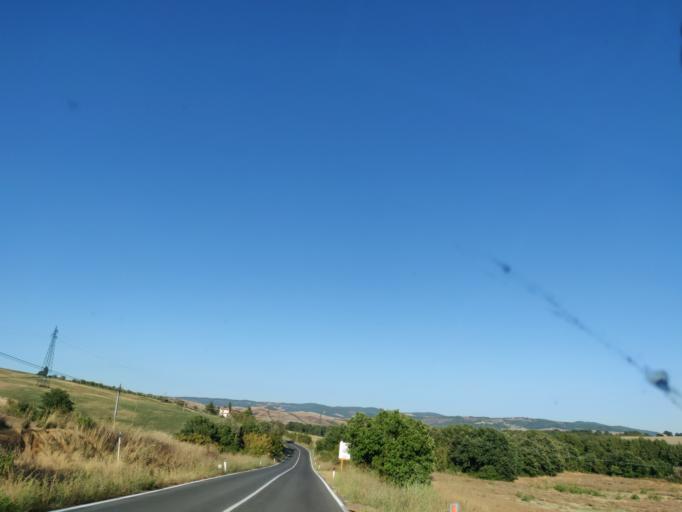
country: IT
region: Tuscany
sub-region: Provincia di Grosseto
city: Castell'Azzara
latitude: 42.8158
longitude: 11.7478
